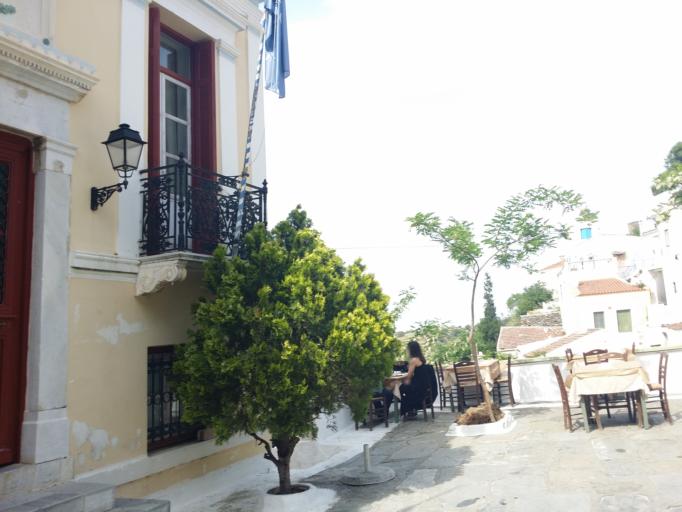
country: GR
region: South Aegean
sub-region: Nomos Kykladon
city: Kea
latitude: 37.6402
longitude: 24.3412
